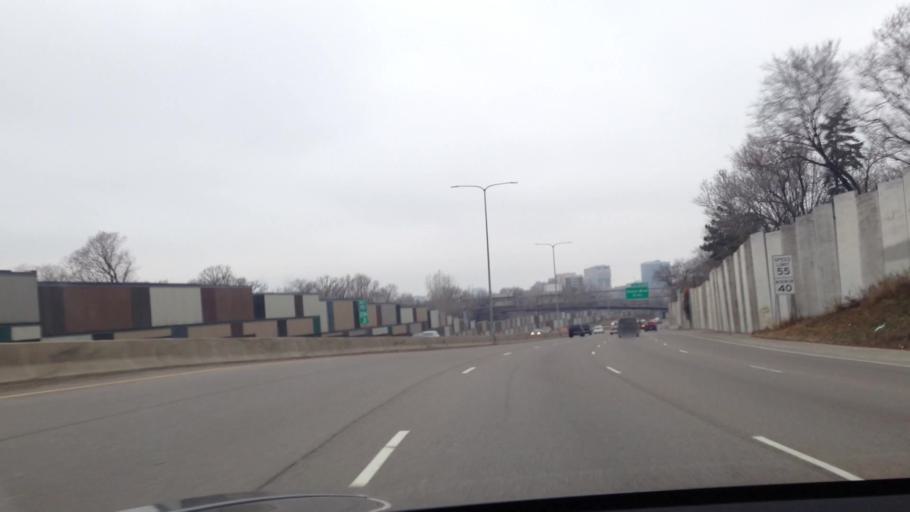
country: US
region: Minnesota
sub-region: Ramsey County
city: Lauderdale
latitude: 44.9604
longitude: -93.2097
